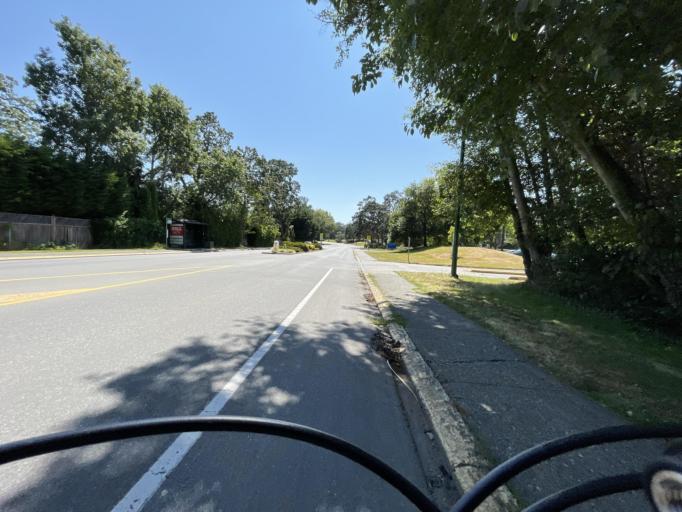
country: CA
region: British Columbia
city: Oak Bay
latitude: 48.4482
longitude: -123.3203
